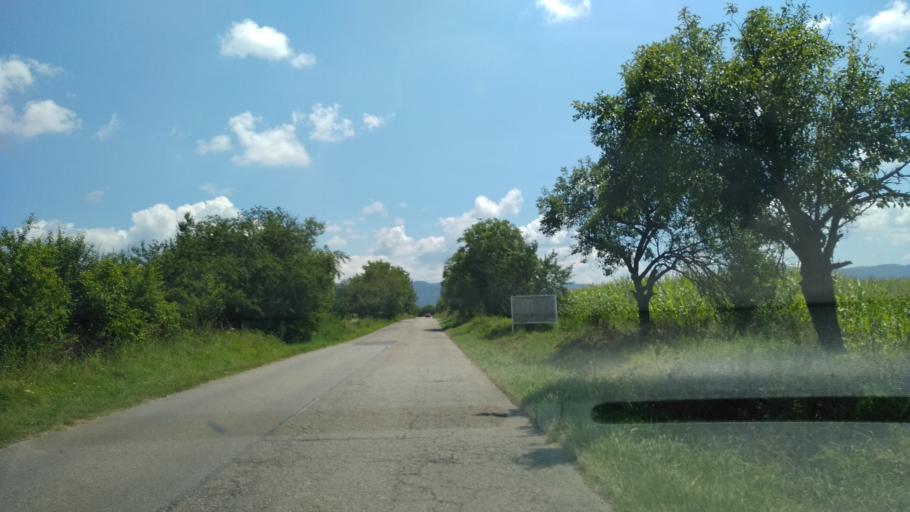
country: RO
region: Hunedoara
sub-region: Comuna Bosorod
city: Bosorod
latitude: 45.7122
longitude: 23.0436
